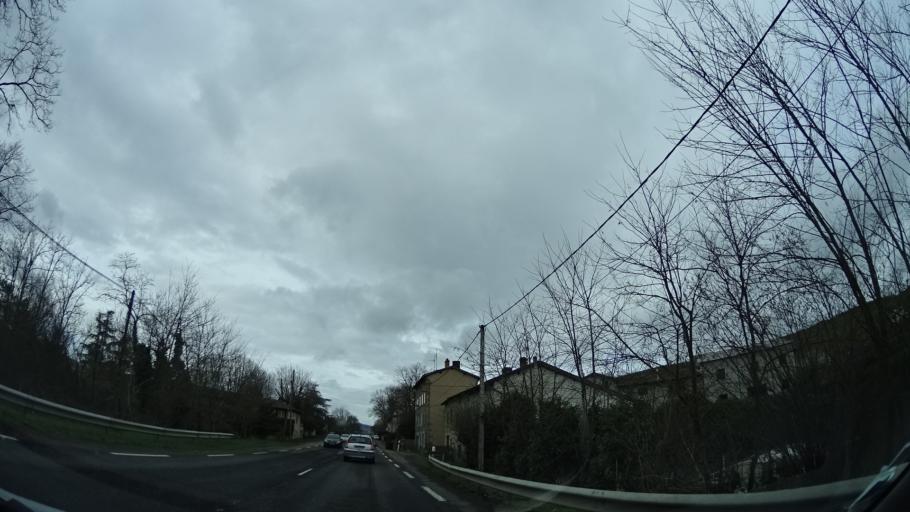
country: FR
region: Rhone-Alpes
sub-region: Departement du Rhone
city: Saint-Romain-de-Popey
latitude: 45.8631
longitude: 4.5546
